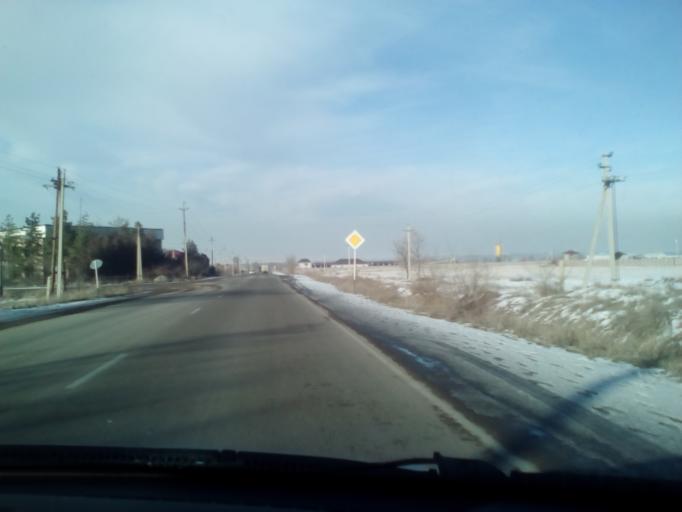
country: KZ
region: Almaty Oblysy
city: Burunday
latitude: 43.1984
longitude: 76.4149
